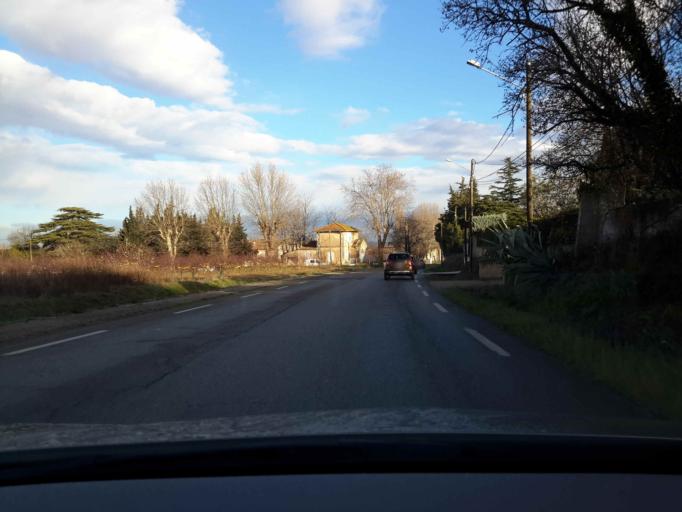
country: FR
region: Languedoc-Roussillon
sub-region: Departement du Gard
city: Generac
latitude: 43.7376
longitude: 4.3441
